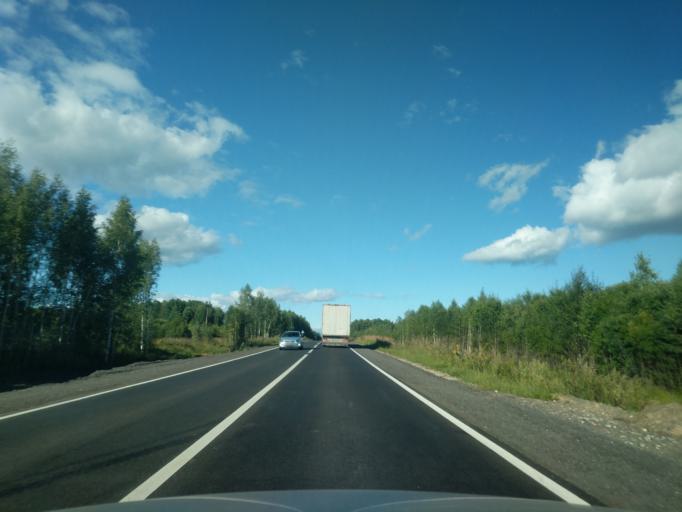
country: RU
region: Kostroma
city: Makar'yev
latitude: 57.9966
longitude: 43.9732
